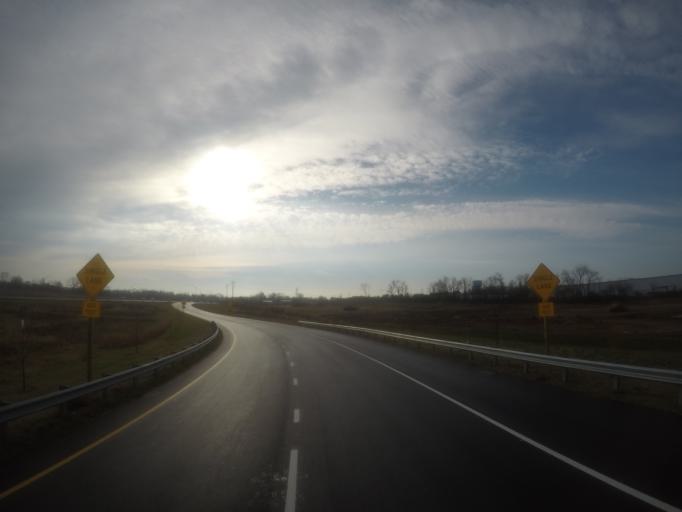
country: US
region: Maryland
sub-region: Frederick County
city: Clover Hill
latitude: 39.4601
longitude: -77.4023
